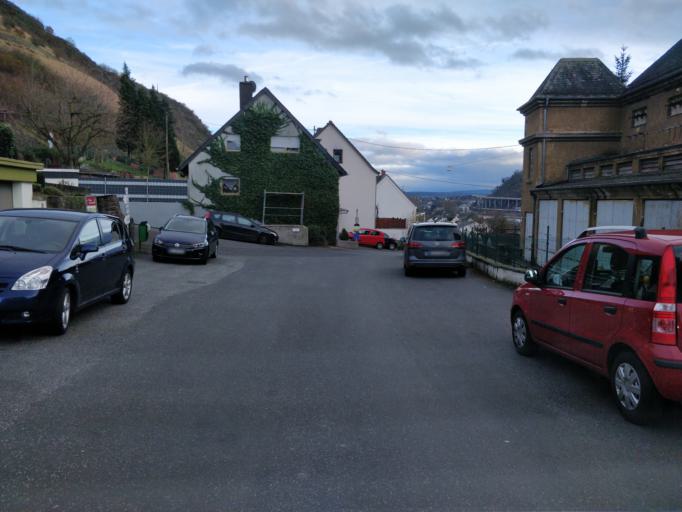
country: DE
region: Rheinland-Pfalz
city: Leutesdorf
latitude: 50.4536
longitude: 7.3859
